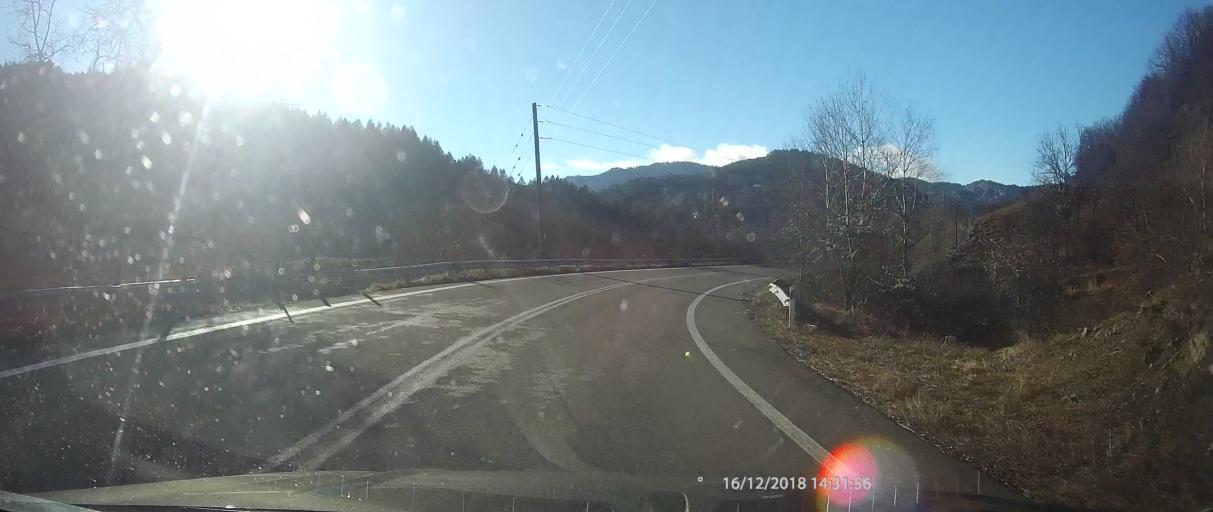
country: GR
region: West Macedonia
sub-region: Nomos Kozanis
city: Tsotili
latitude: 40.1950
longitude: 21.1765
